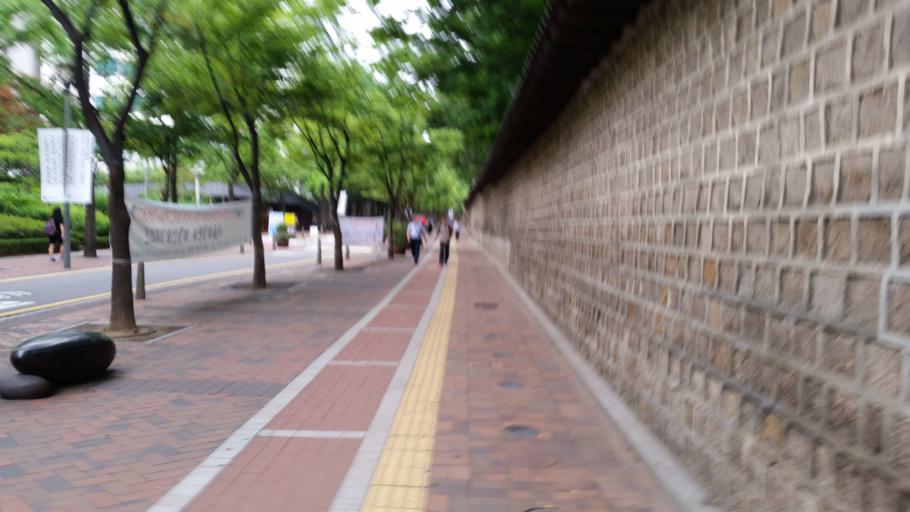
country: KR
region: Seoul
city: Seoul
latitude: 37.5649
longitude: 126.9757
